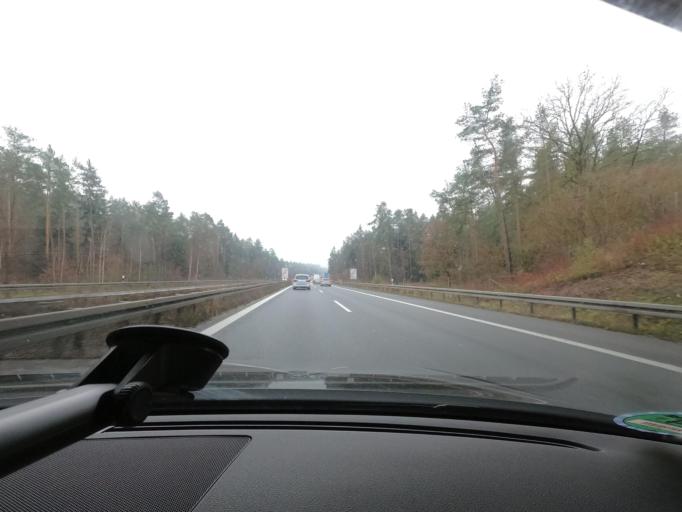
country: DE
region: Bavaria
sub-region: Upper Franconia
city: Memmelsdorf
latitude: 49.8884
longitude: 10.9494
